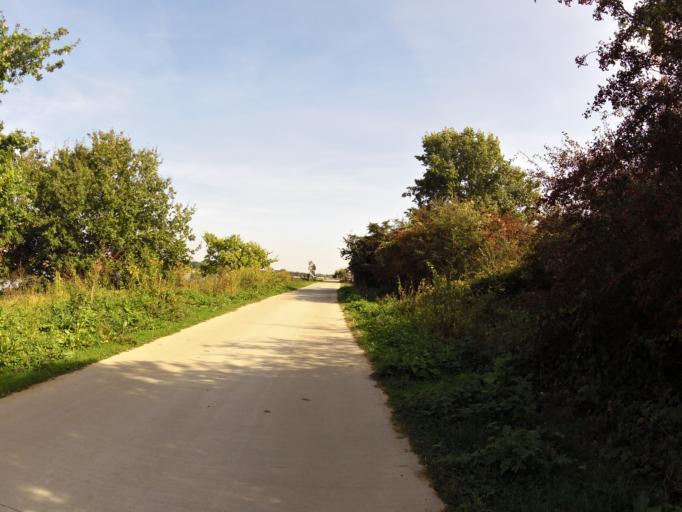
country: NL
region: Gelderland
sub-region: Gemeente Duiven
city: Duiven
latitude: 51.8797
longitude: 6.0160
